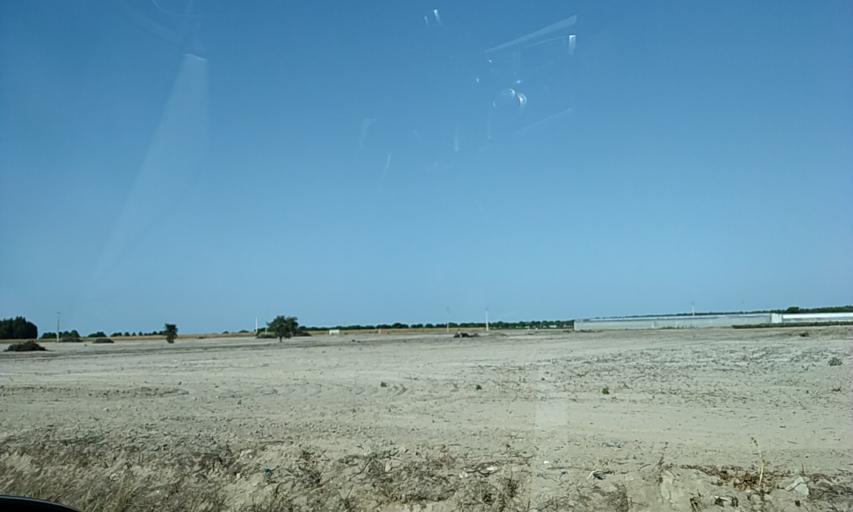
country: PT
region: Santarem
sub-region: Almeirim
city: Almeirim
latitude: 39.1679
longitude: -8.6206
